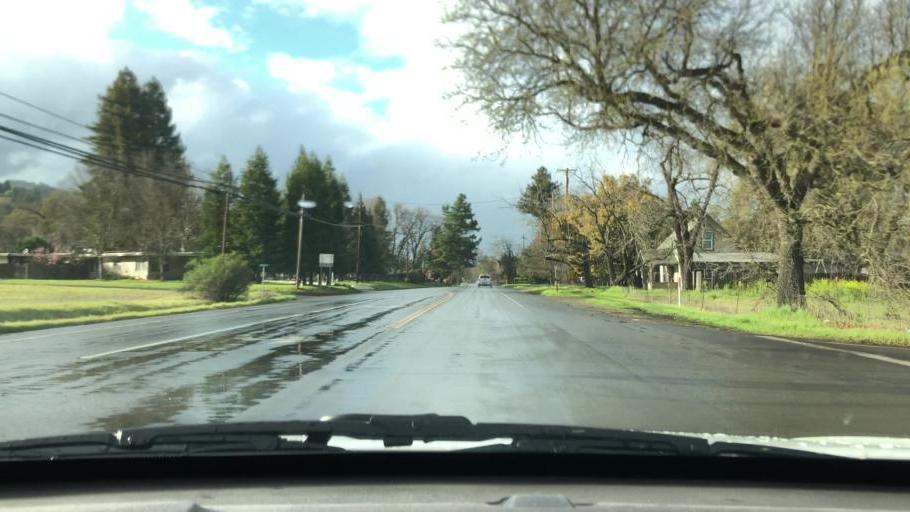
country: US
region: California
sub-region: Mendocino County
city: Talmage
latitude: 39.1119
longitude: -123.1978
